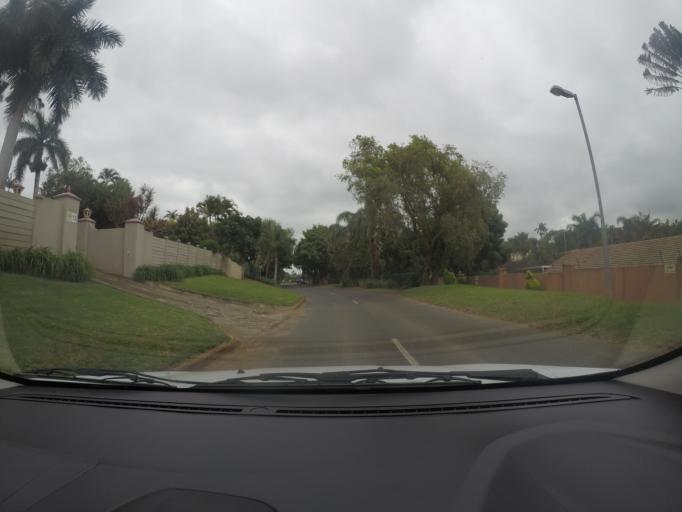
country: ZA
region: KwaZulu-Natal
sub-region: uThungulu District Municipality
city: Empangeni
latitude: -28.7616
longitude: 31.8896
